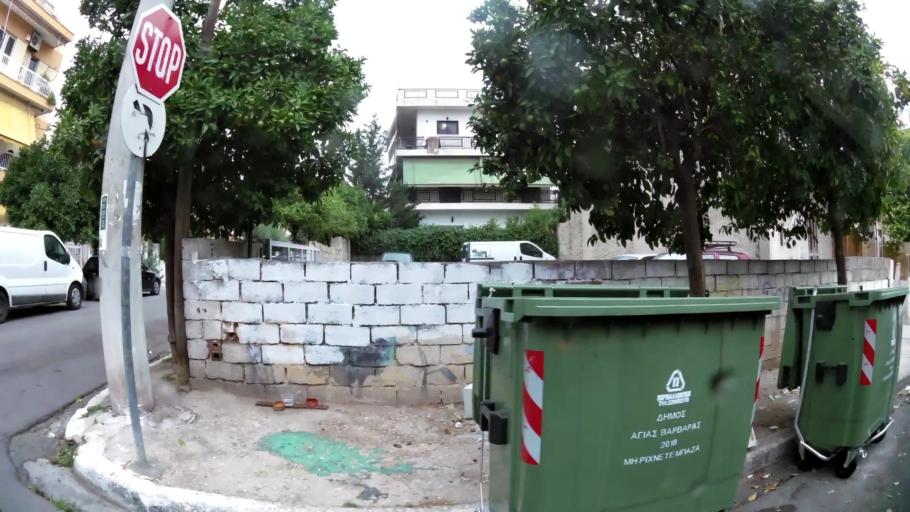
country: GR
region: Attica
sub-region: Nomarchia Athinas
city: Agia Varvara
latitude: 37.9902
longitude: 23.6612
